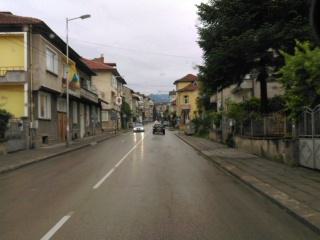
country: BG
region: Lovech
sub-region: Obshtina Troyan
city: Troyan
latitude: 42.8887
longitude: 24.7102
